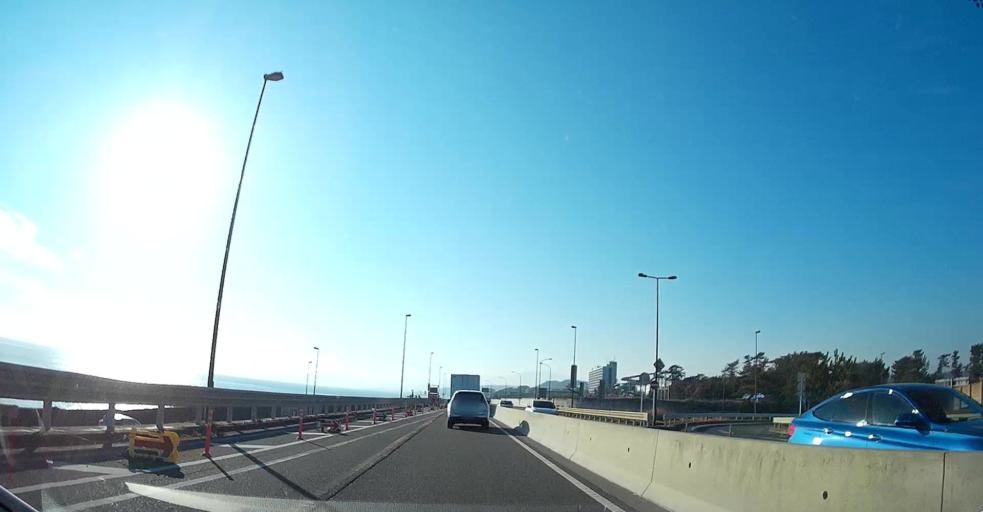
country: JP
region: Kanagawa
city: Oiso
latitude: 35.3012
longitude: 139.2878
